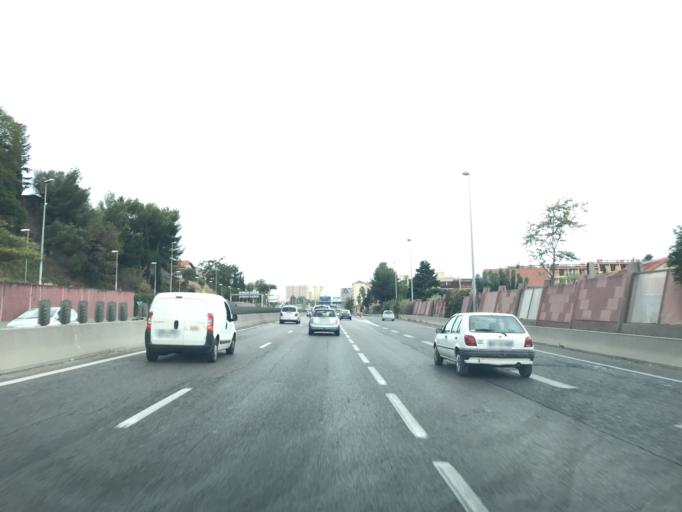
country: FR
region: Provence-Alpes-Cote d'Azur
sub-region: Departement du Var
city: La Valette-du-Var
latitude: 43.1236
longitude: 5.9599
